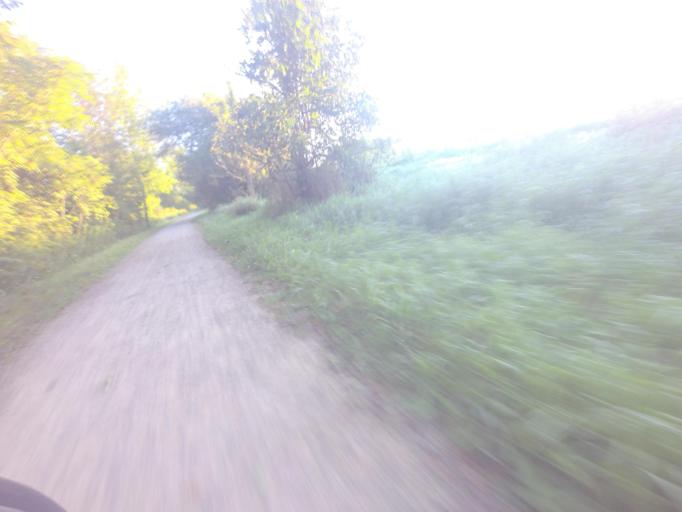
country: CA
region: Ontario
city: Bradford West Gwillimbury
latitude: 44.0089
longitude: -79.8108
